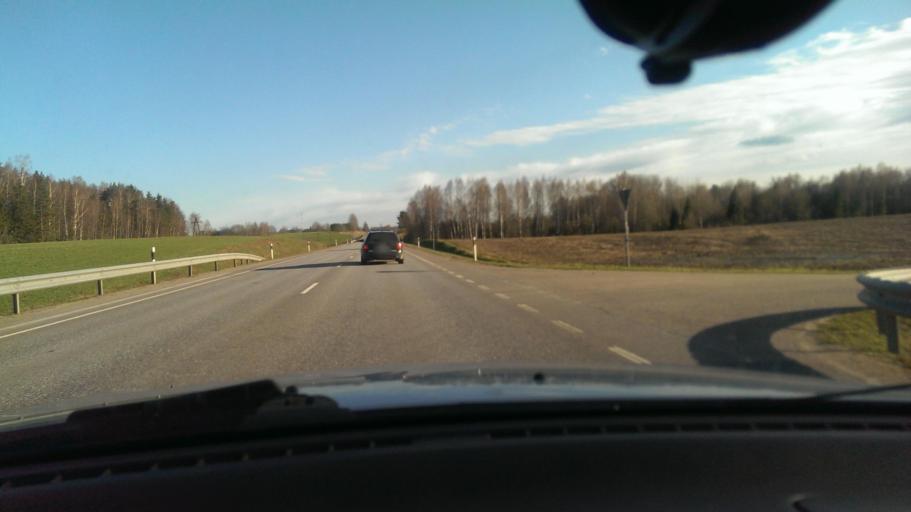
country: EE
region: Tartu
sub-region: UElenurme vald
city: Ulenurme
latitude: 58.1694
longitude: 26.6916
